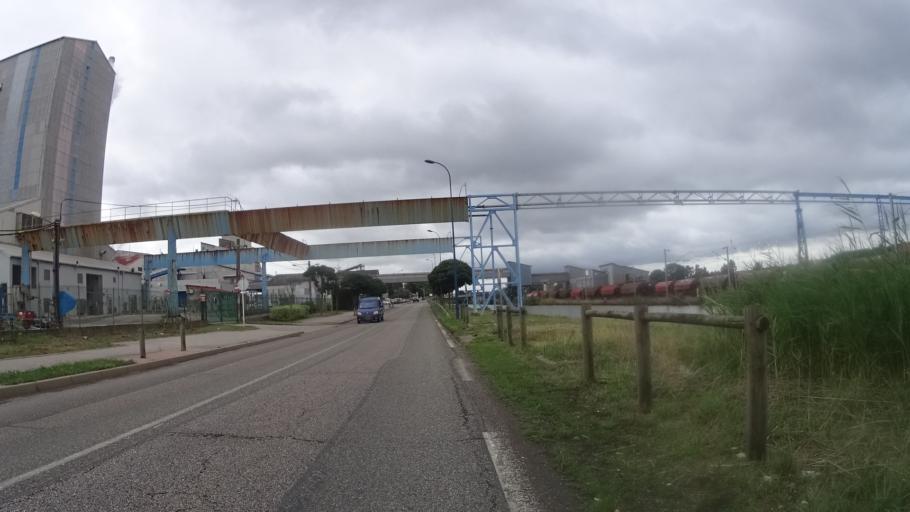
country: FR
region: Lorraine
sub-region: Departement de Meurthe-et-Moselle
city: Saint-Nicolas-de-Port
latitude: 48.6376
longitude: 6.3068
